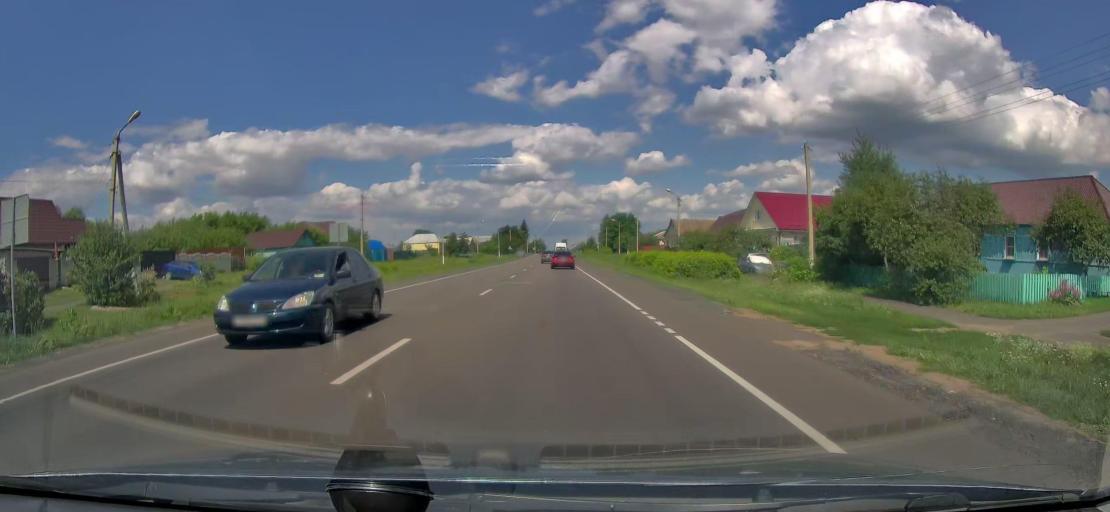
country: RU
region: Kursk
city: Zolotukhino
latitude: 51.9275
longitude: 36.3053
